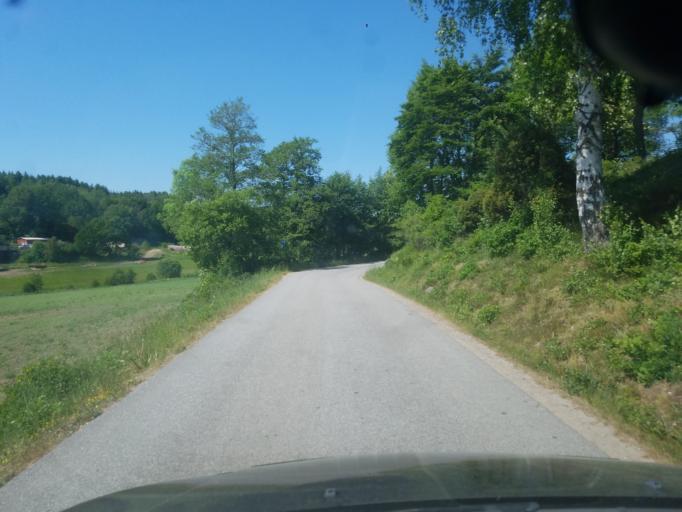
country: SE
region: Vaestra Goetaland
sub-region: Orust
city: Henan
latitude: 58.2717
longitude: 11.5723
